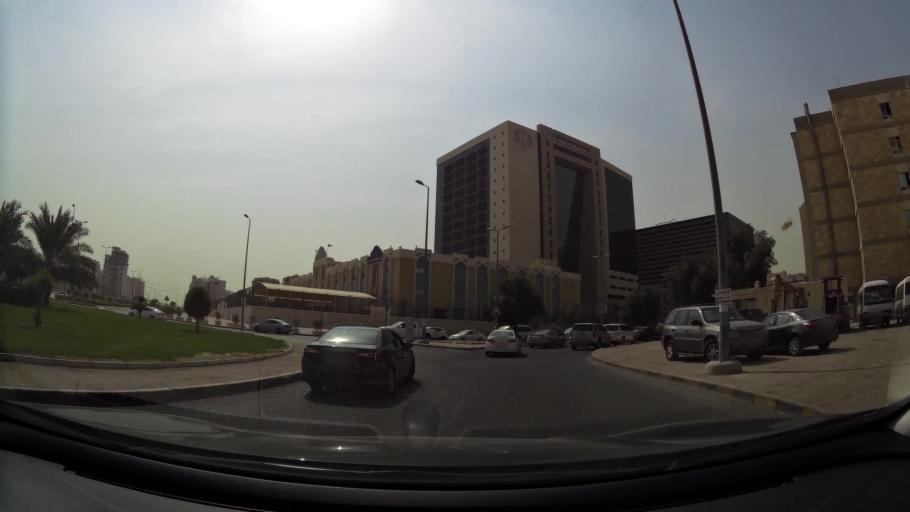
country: KW
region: Al Asimah
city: Ar Rabiyah
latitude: 29.3056
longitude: 47.9149
